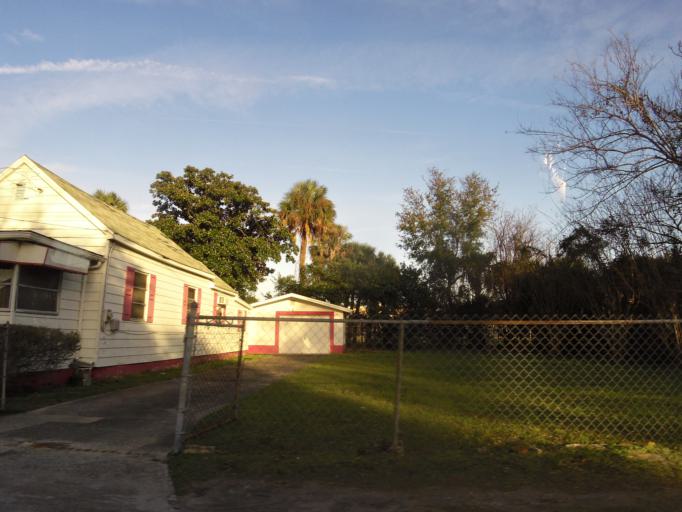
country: US
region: Florida
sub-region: Duval County
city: Jacksonville
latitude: 30.3355
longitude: -81.6442
